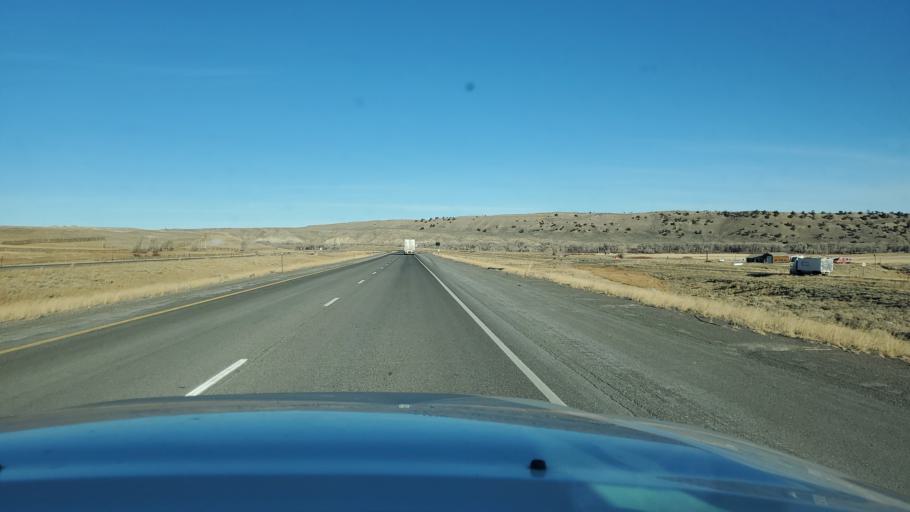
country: US
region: Wyoming
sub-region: Carbon County
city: Saratoga
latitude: 41.6899
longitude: -106.3818
